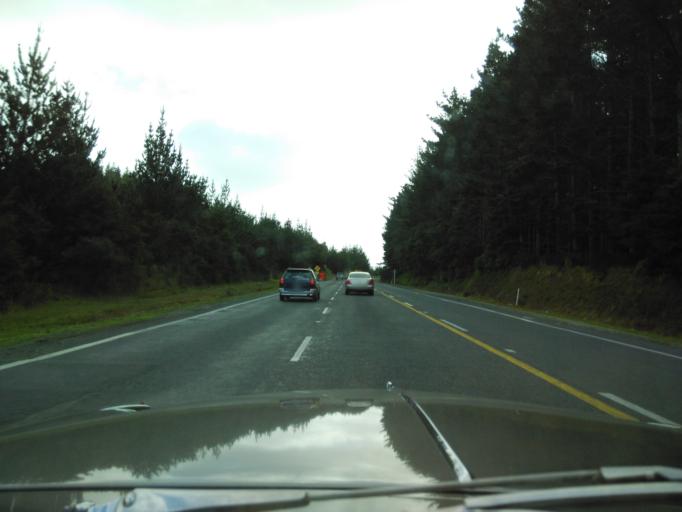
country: NZ
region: Auckland
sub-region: Auckland
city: Wellsford
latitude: -36.2295
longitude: 174.4929
